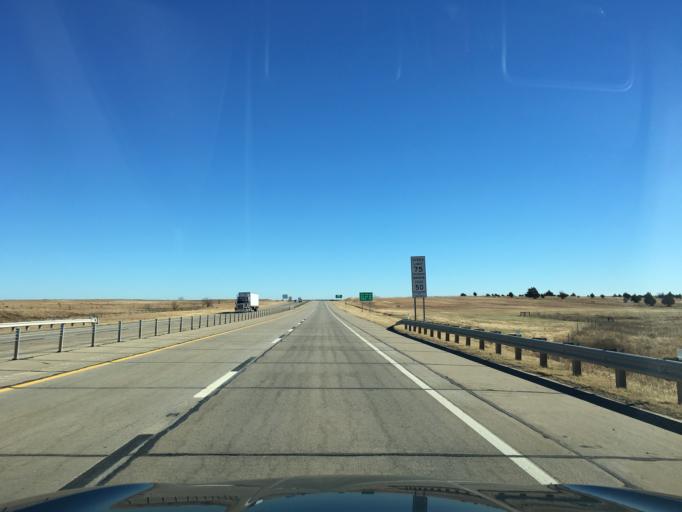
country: US
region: Oklahoma
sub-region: Noble County
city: Perry
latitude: 36.3999
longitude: -97.3117
